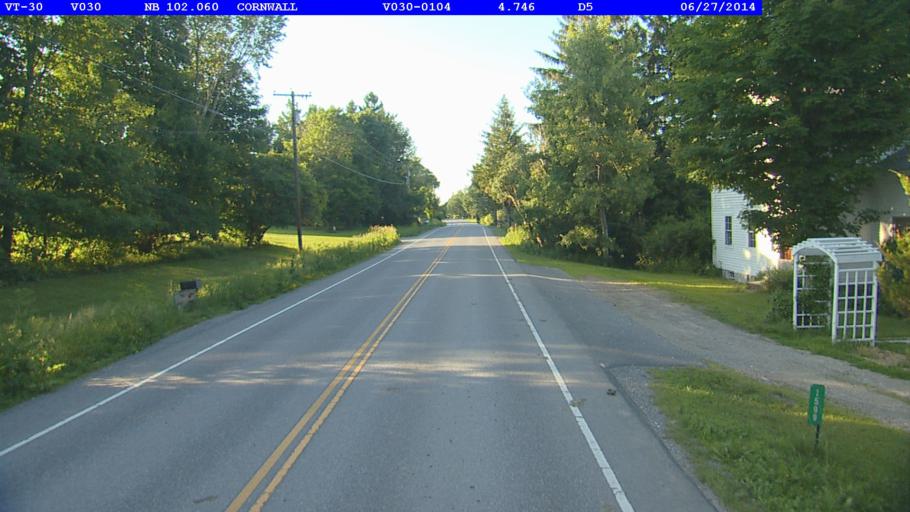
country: US
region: Vermont
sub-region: Addison County
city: Middlebury (village)
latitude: 43.9757
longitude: -73.2054
